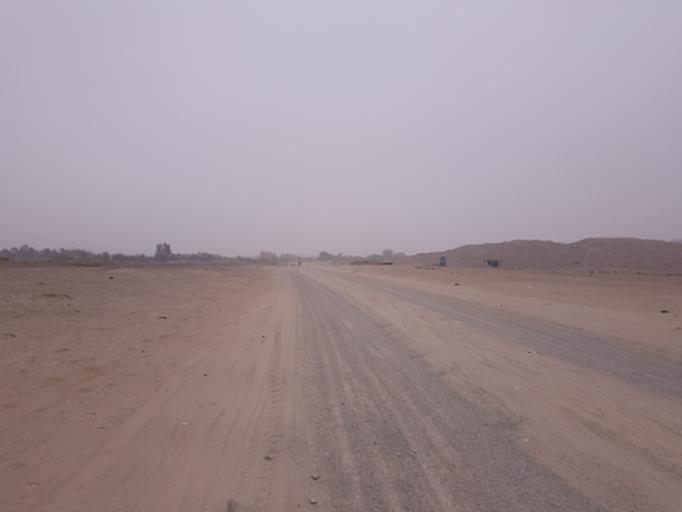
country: PE
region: Lima
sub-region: Lima
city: Santa Maria
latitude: -11.9839
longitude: -76.9099
